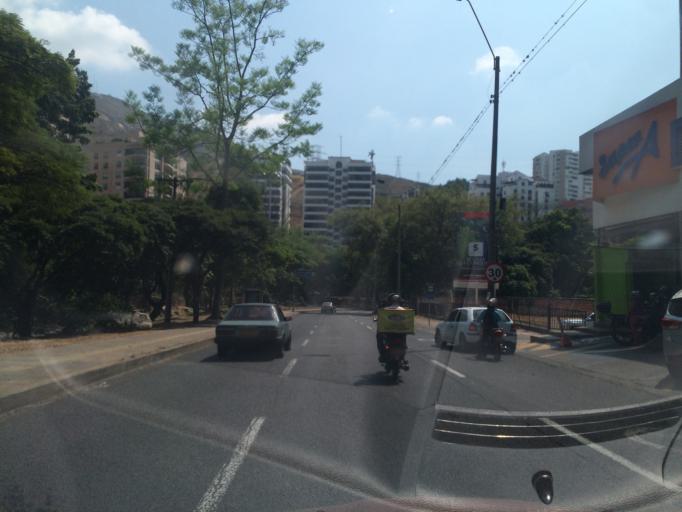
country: CO
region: Valle del Cauca
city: Cali
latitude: 3.4534
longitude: -76.5482
